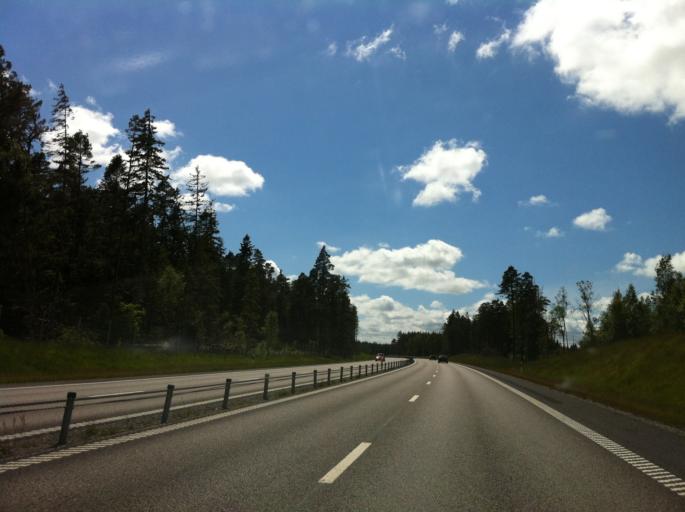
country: SE
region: Vaestra Goetaland
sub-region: Trollhattan
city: Sjuntorp
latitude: 58.2350
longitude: 12.2271
